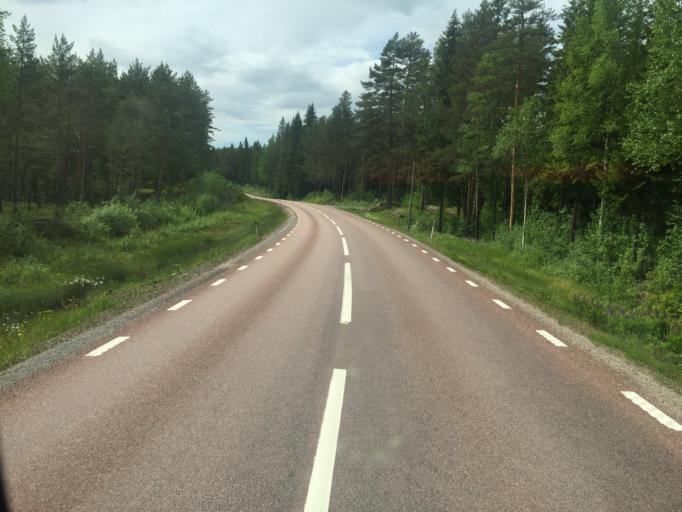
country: SE
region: Dalarna
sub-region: Vansbro Kommun
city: Vansbro
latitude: 60.5052
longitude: 14.1765
